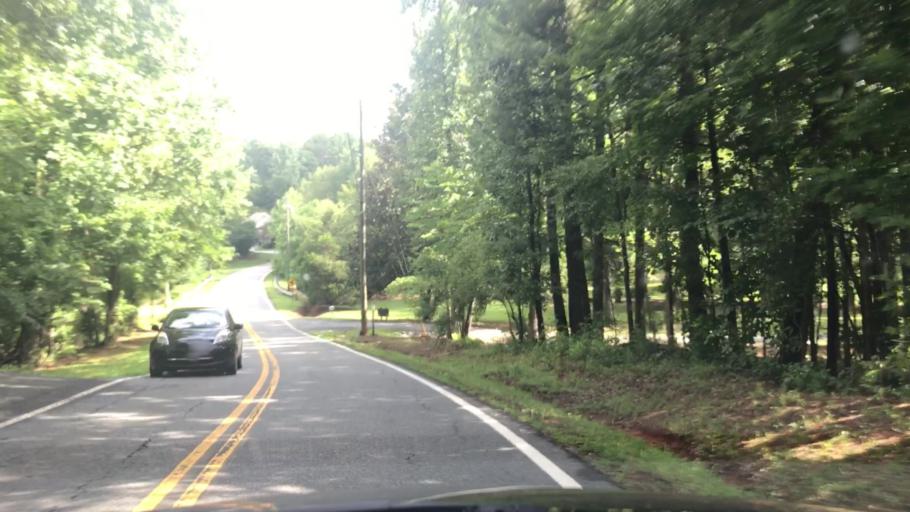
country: US
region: Georgia
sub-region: Fulton County
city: Johns Creek
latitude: 34.1236
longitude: -84.2005
